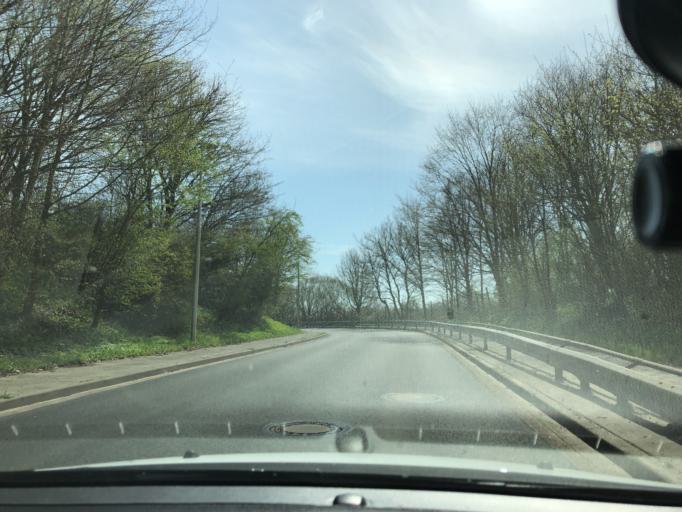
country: DE
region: Schleswig-Holstein
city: Flensburg
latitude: 54.7736
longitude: 9.4467
